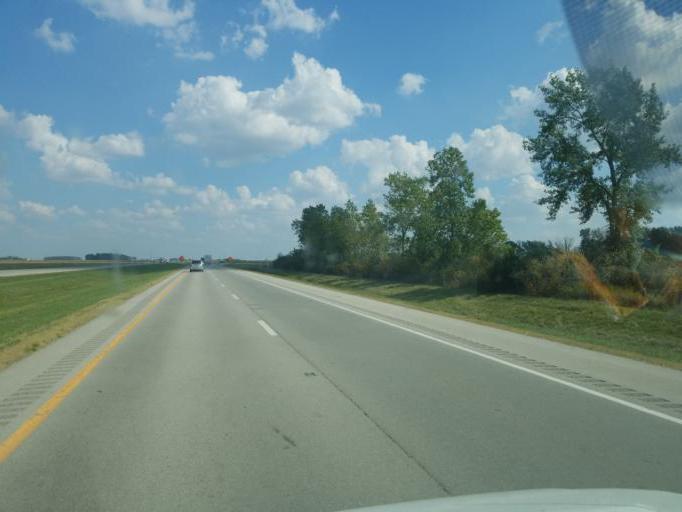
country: US
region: Ohio
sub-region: Van Wert County
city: Van Wert
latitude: 40.8851
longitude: -84.5502
